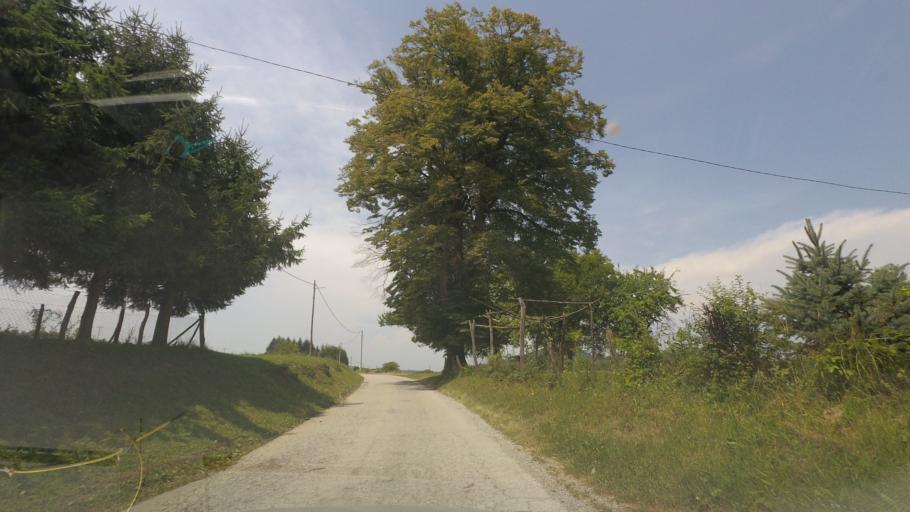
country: HR
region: Karlovacka
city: Vojnic
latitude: 45.3878
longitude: 15.6049
